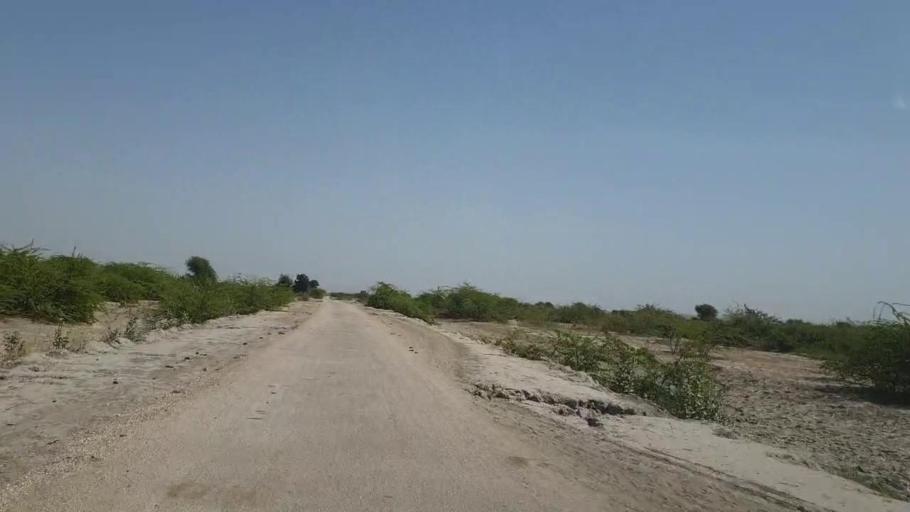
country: PK
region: Sindh
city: Naukot
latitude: 24.9569
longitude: 69.5109
